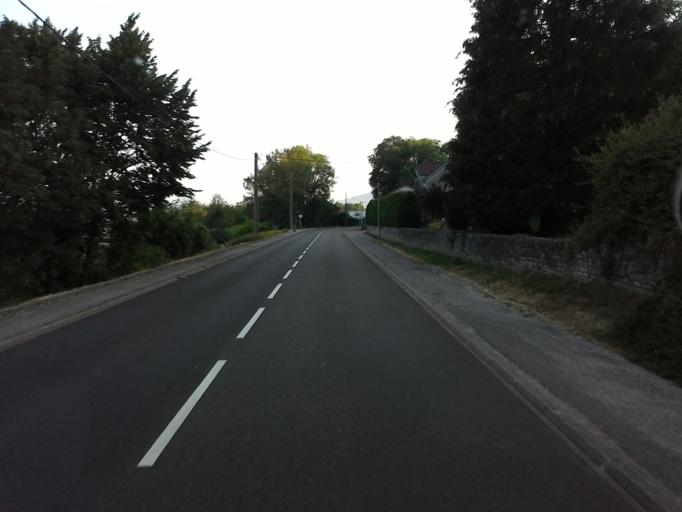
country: FR
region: Franche-Comte
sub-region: Departement de la Haute-Saone
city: Echenoz-la-Meline
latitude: 47.5950
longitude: 6.1390
